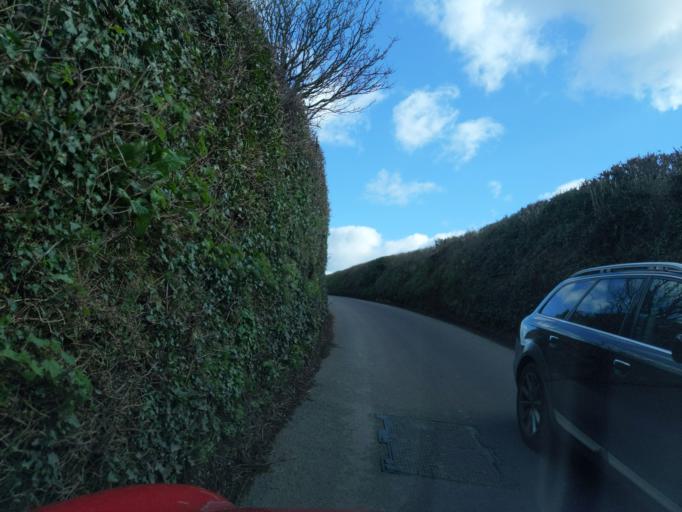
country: GB
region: England
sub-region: Devon
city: Salcombe
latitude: 50.2659
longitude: -3.7211
